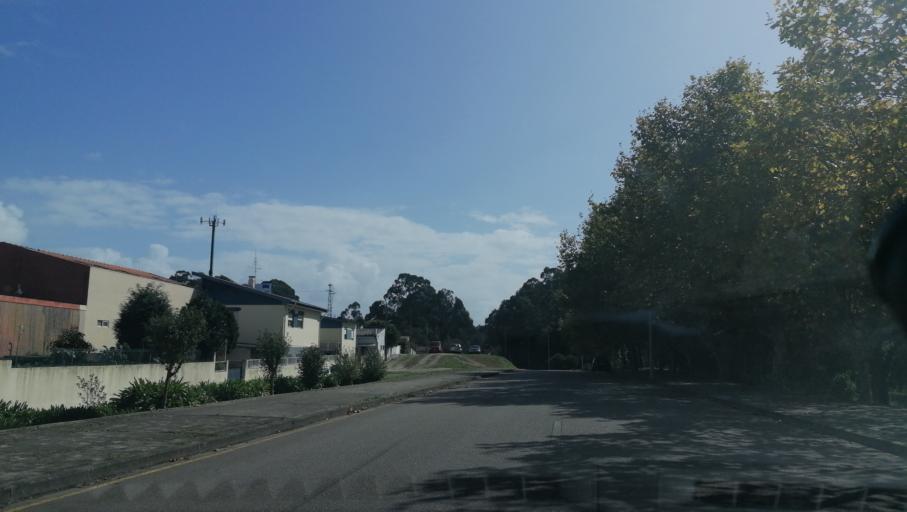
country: PT
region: Aveiro
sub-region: Espinho
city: Silvalde
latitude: 40.9992
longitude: -8.6205
